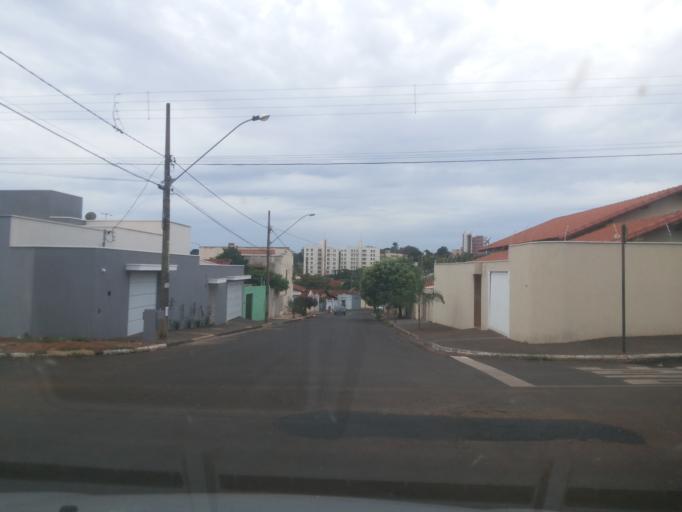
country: BR
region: Minas Gerais
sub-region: Ituiutaba
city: Ituiutaba
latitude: -18.9691
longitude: -49.4716
